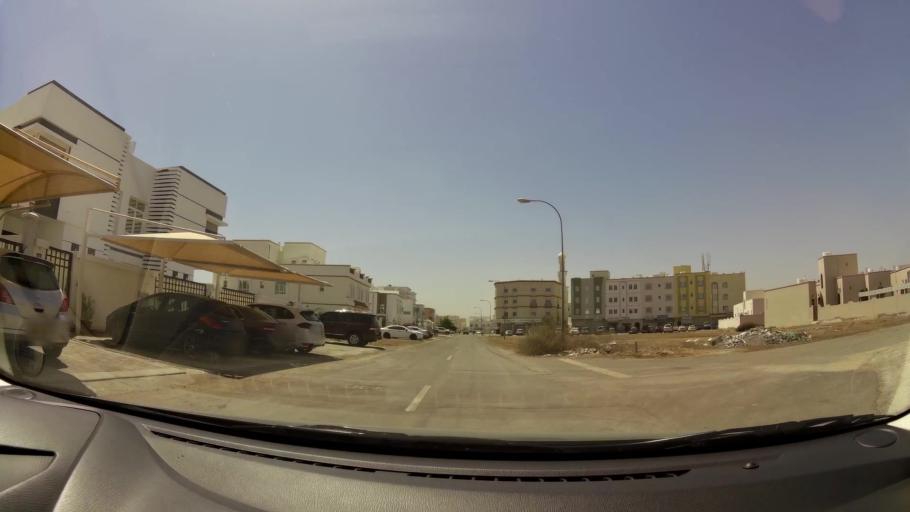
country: OM
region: Muhafazat Masqat
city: As Sib al Jadidah
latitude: 23.6253
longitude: 58.2554
